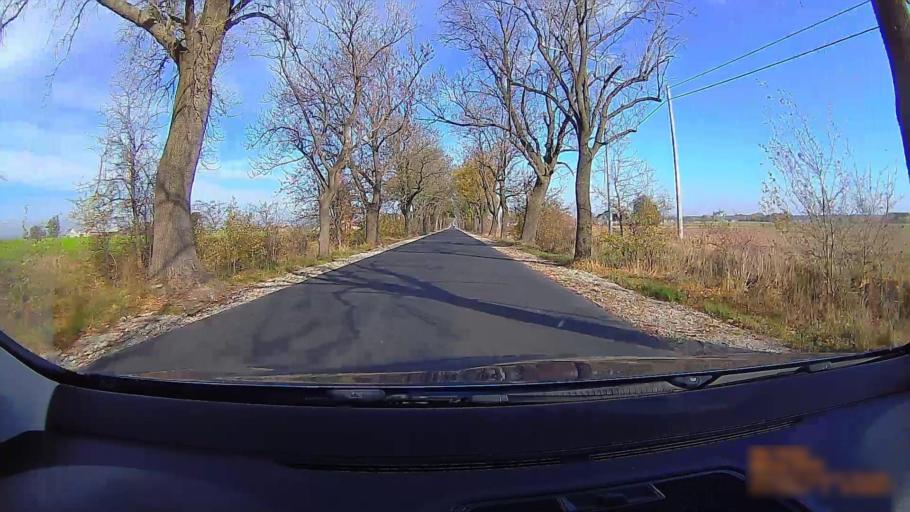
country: PL
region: Greater Poland Voivodeship
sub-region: Powiat ostrzeszowski
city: Doruchow
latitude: 51.3998
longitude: 18.0636
